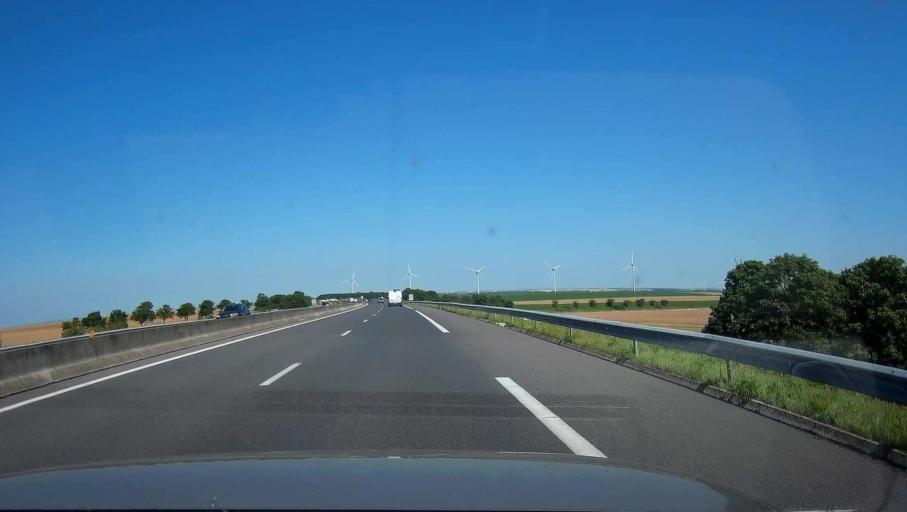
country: FR
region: Champagne-Ardenne
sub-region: Departement de la Marne
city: Compertrix
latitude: 48.8115
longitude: 4.2884
